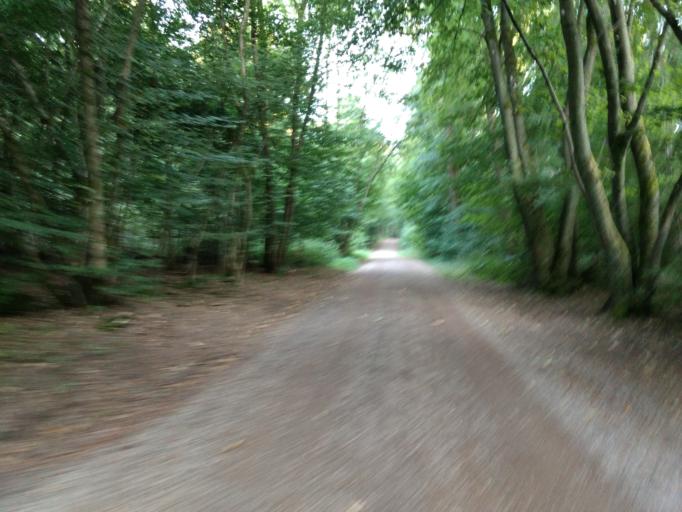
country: DE
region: Saarland
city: Nalbach
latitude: 49.4035
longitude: 6.7831
